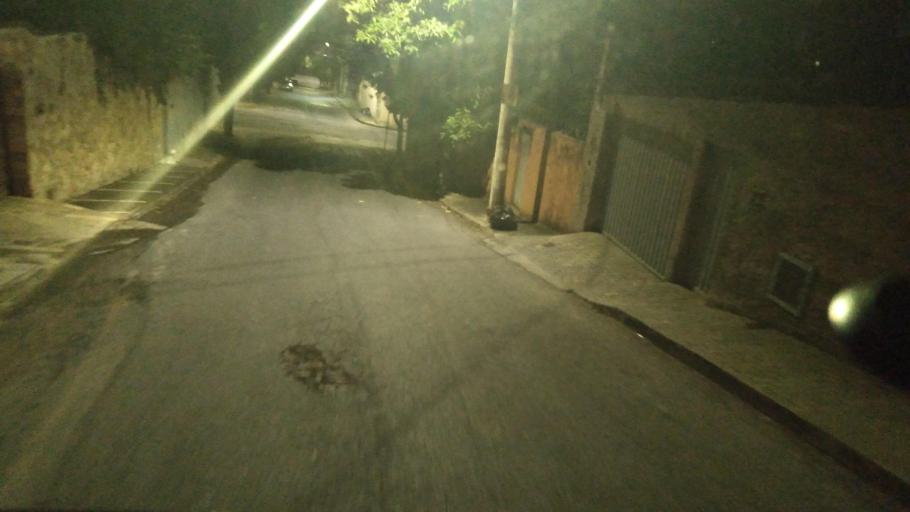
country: BR
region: Minas Gerais
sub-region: Belo Horizonte
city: Belo Horizonte
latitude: -19.8888
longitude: -43.9590
